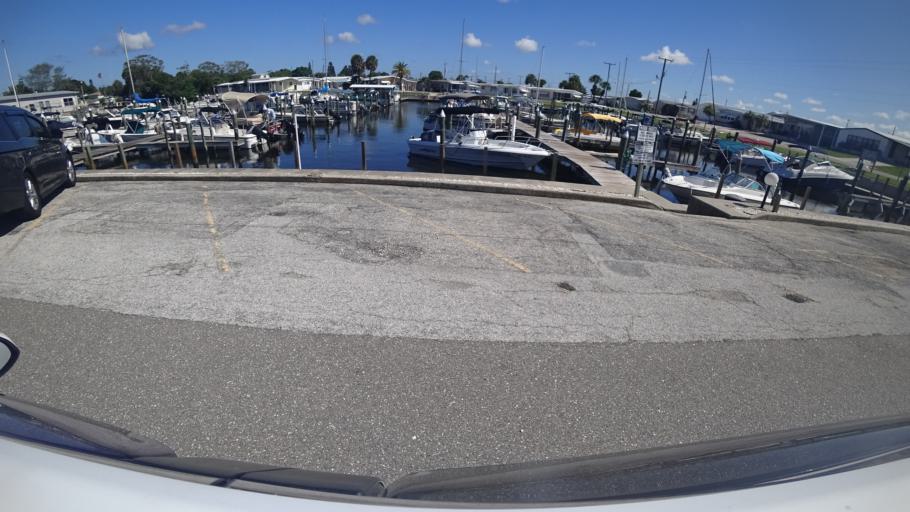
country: US
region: Florida
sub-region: Manatee County
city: Bayshore Gardens
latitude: 27.4193
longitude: -82.5841
